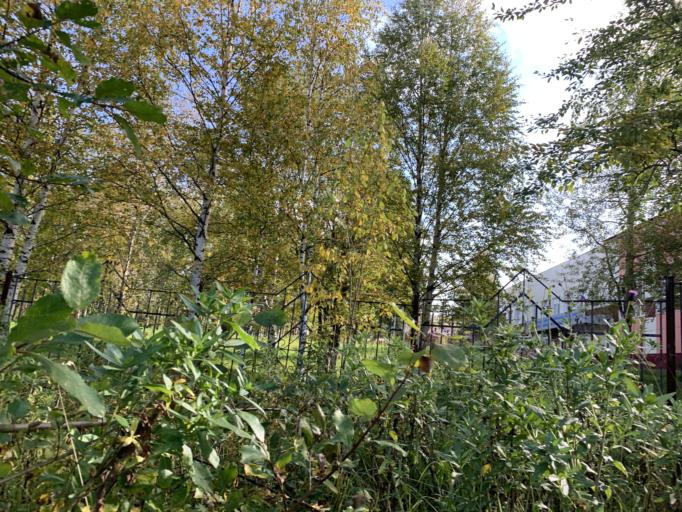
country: RU
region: Perm
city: Gubakha
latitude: 58.8368
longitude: 57.5587
